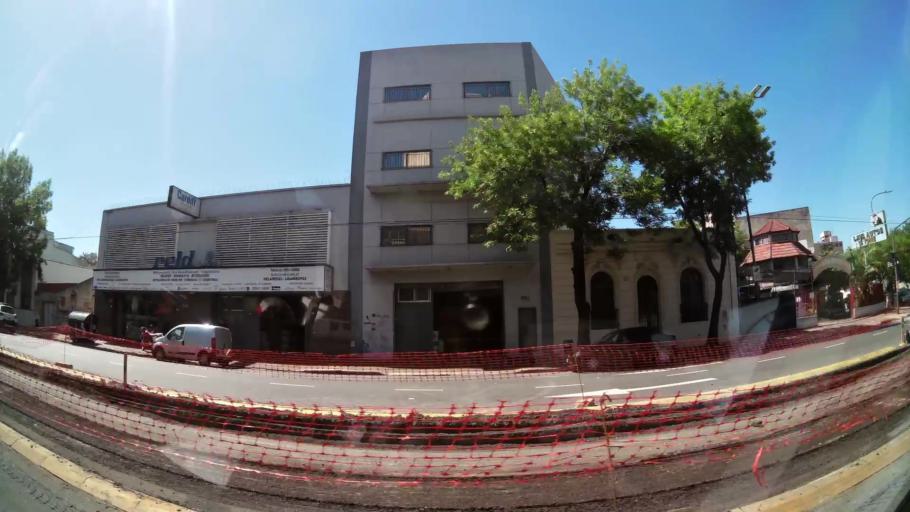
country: AR
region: Buenos Aires F.D.
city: Buenos Aires
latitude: -34.6330
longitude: -58.4094
